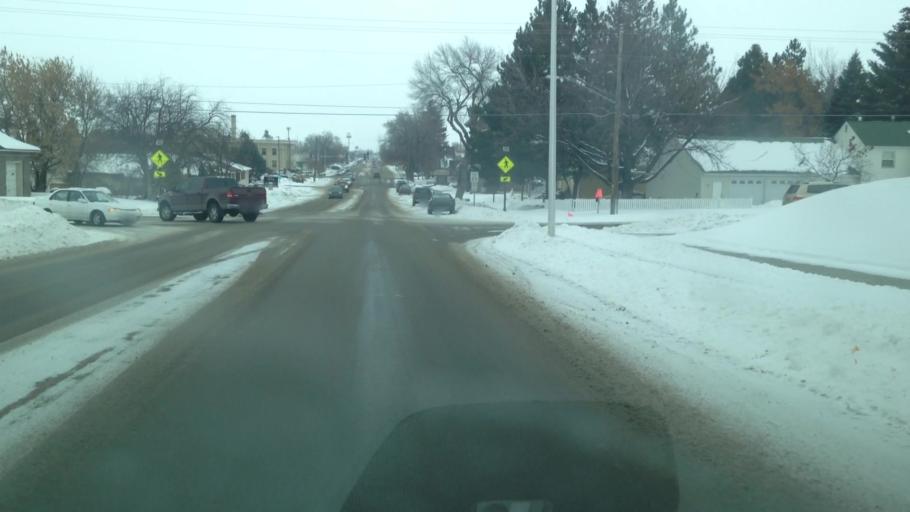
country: US
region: Idaho
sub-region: Madison County
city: Rexburg
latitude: 43.8236
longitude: -111.7781
